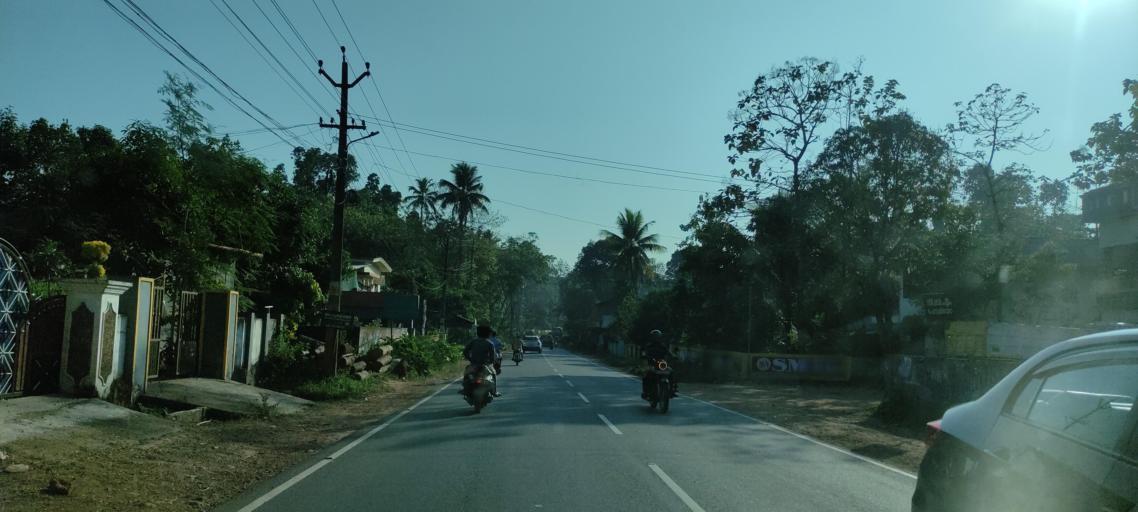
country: IN
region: Kerala
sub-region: Pattanamtitta
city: Adur
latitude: 9.1679
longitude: 76.6597
